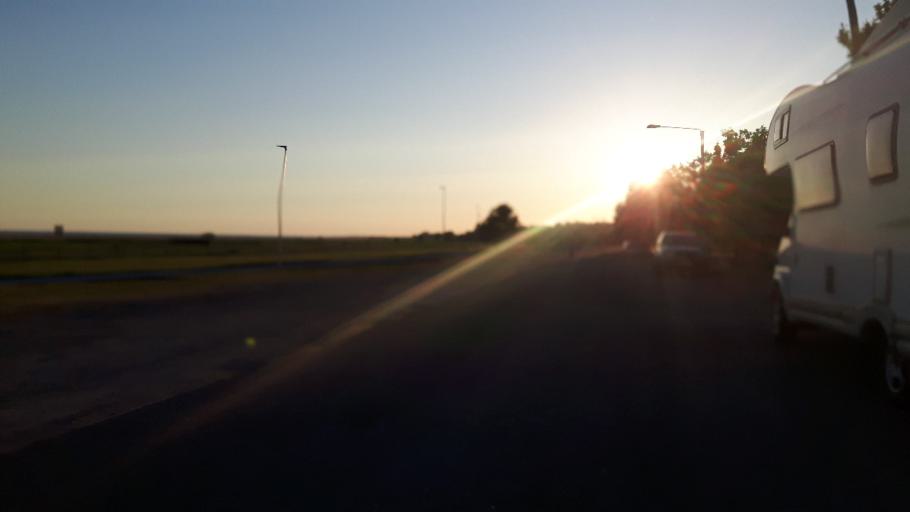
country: EE
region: Paernumaa
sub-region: Paernu linn
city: Parnu
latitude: 58.3668
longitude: 24.5388
